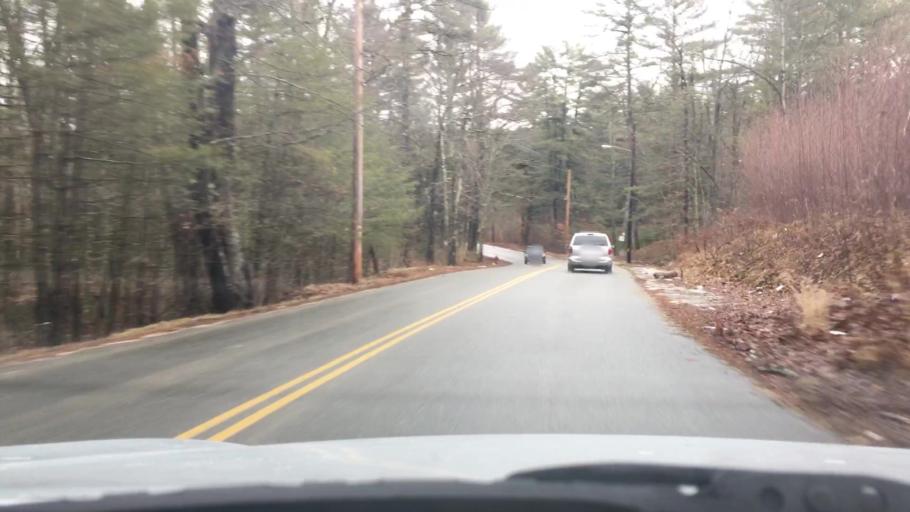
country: US
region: Massachusetts
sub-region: Worcester County
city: Athol
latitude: 42.5746
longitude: -72.2564
